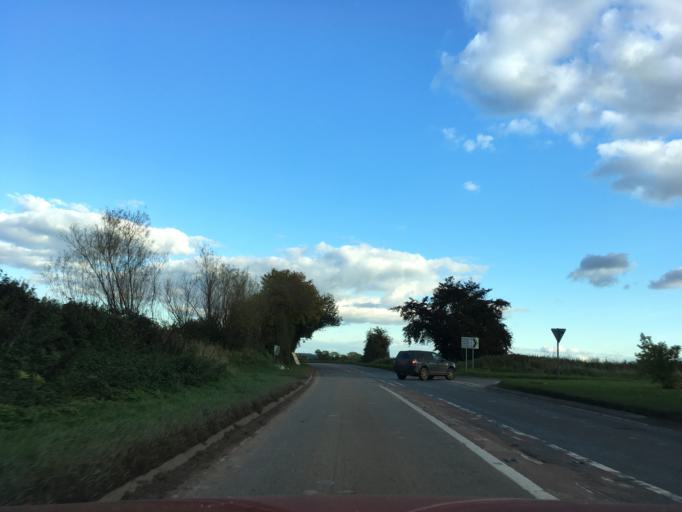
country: GB
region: England
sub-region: Herefordshire
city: Yatton
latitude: 52.0497
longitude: -2.5139
